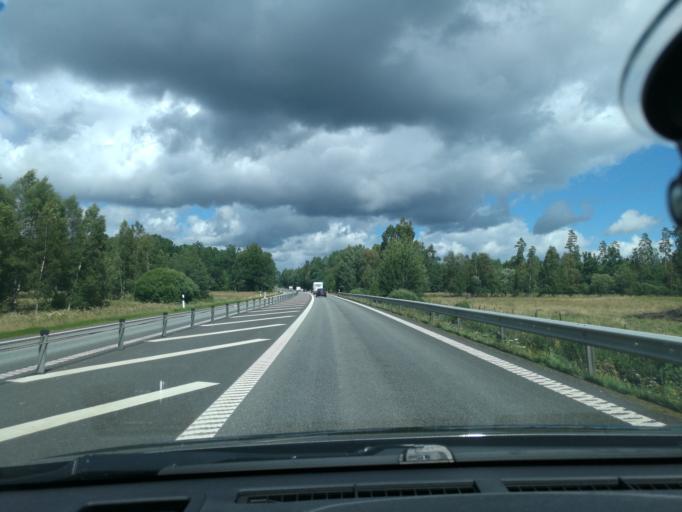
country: SE
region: Skane
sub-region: Osby Kommun
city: Osby
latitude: 56.3755
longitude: 14.0346
